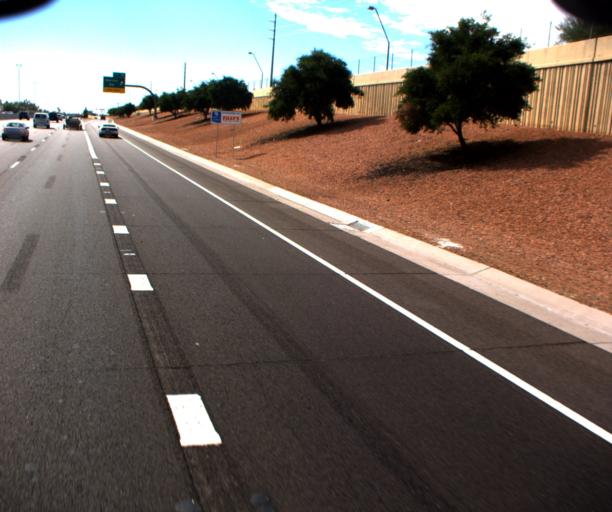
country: US
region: Arizona
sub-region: Maricopa County
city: San Carlos
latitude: 33.3416
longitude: -111.8935
